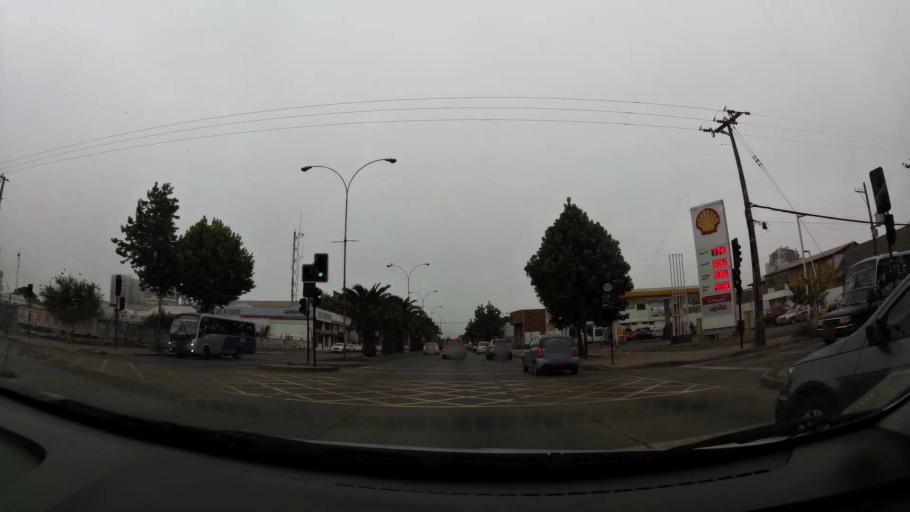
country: CL
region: Biobio
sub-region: Provincia de Concepcion
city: Concepcion
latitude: -36.8260
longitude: -73.0582
